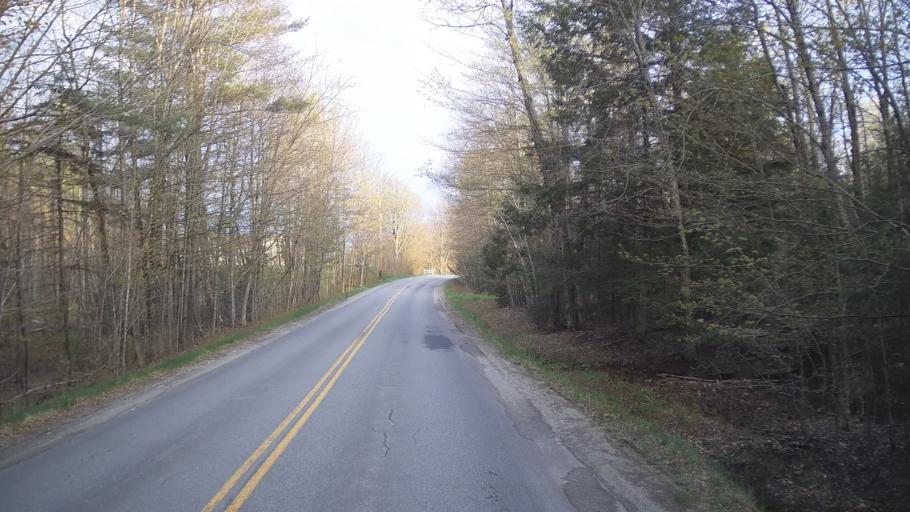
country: US
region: Vermont
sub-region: Orleans County
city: Newport
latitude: 44.9286
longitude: -72.4340
